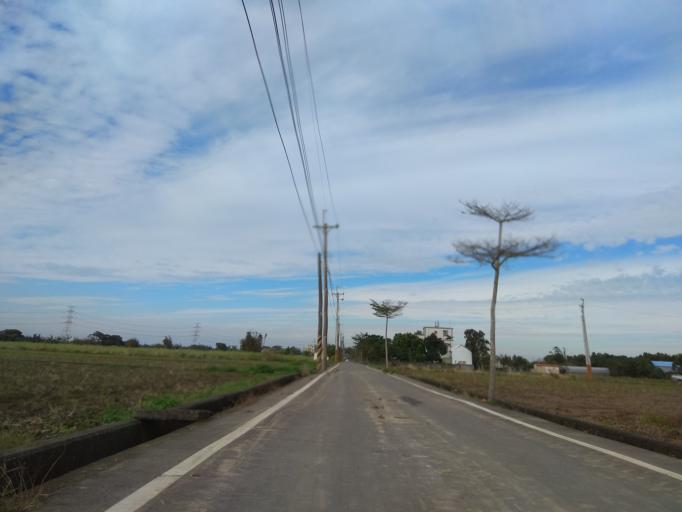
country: TW
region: Taiwan
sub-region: Hsinchu
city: Zhubei
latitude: 24.9516
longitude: 121.1110
